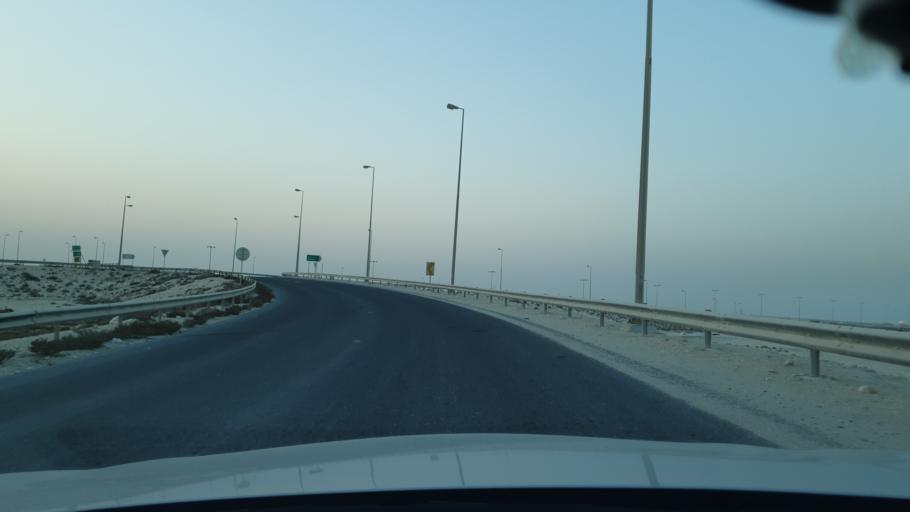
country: BH
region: Central Governorate
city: Dar Kulayb
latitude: 25.9561
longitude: 50.5964
